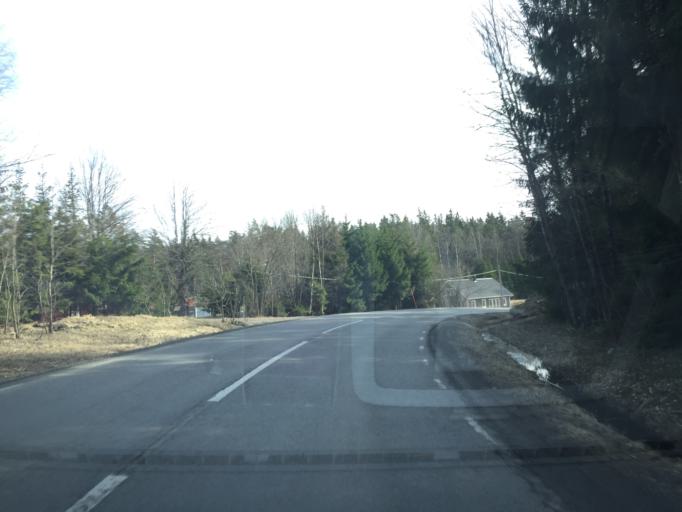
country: SE
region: Stockholm
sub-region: Haninge Kommun
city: Jordbro
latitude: 59.1235
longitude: 18.0111
